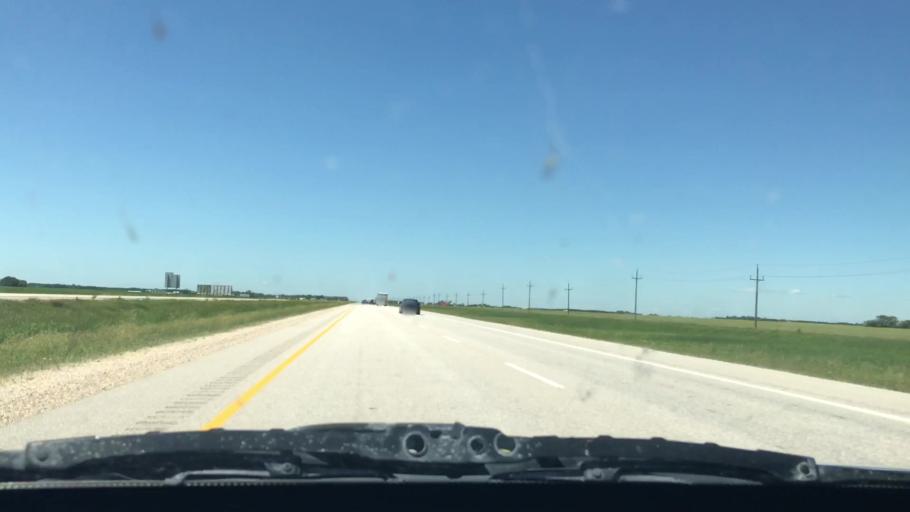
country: CA
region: Manitoba
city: Steinbach
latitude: 49.7131
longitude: -96.6748
